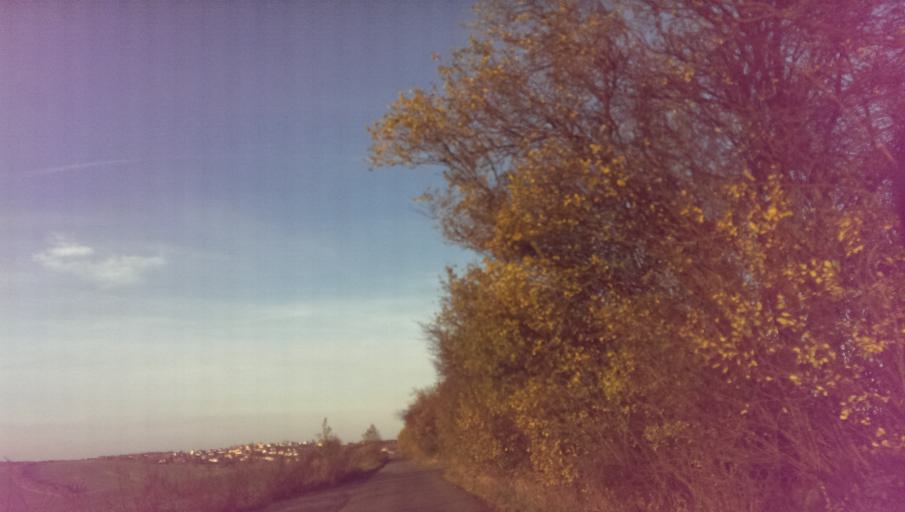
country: CZ
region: Zlin
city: Brezolupy
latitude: 49.1537
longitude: 17.5997
